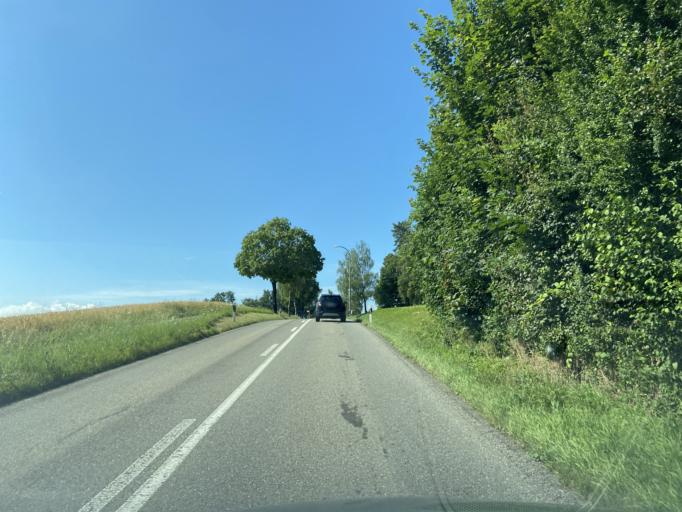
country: CH
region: Zurich
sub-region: Bezirk Meilen
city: Oetwil am See
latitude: 47.2653
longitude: 8.7138
